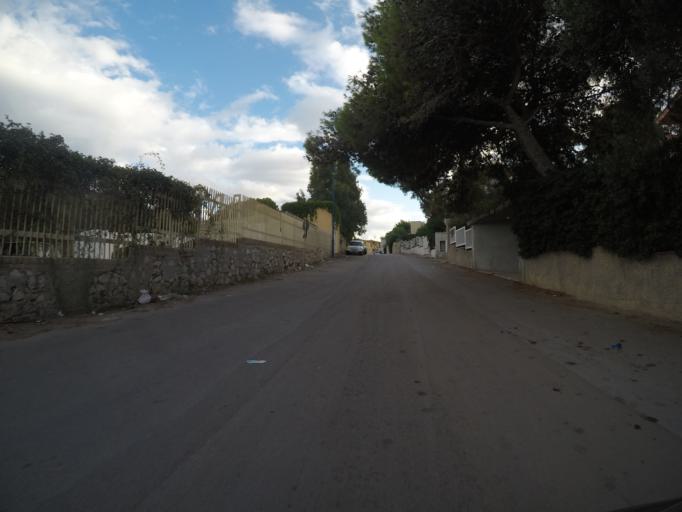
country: IT
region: Sicily
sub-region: Palermo
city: Palermo
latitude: 38.2113
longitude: 13.3277
